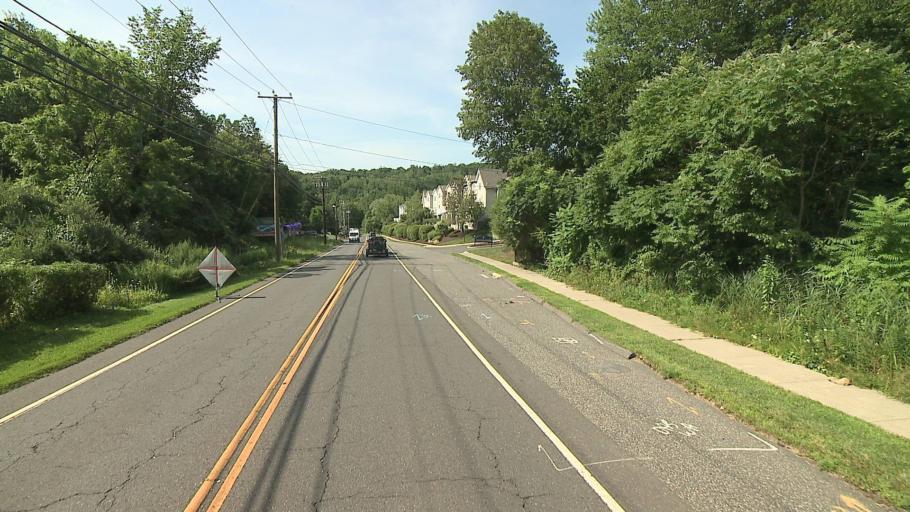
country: US
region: Connecticut
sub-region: Fairfield County
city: Danbury
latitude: 41.4277
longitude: -73.4719
